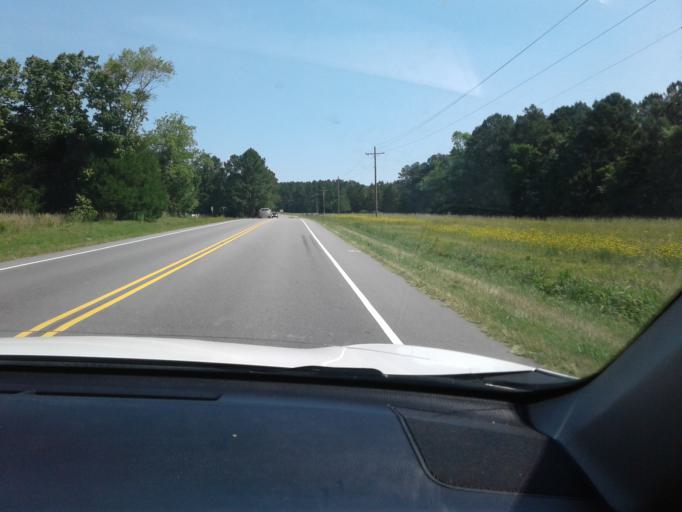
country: US
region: North Carolina
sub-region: Harnett County
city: Lillington
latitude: 35.4379
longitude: -78.8285
